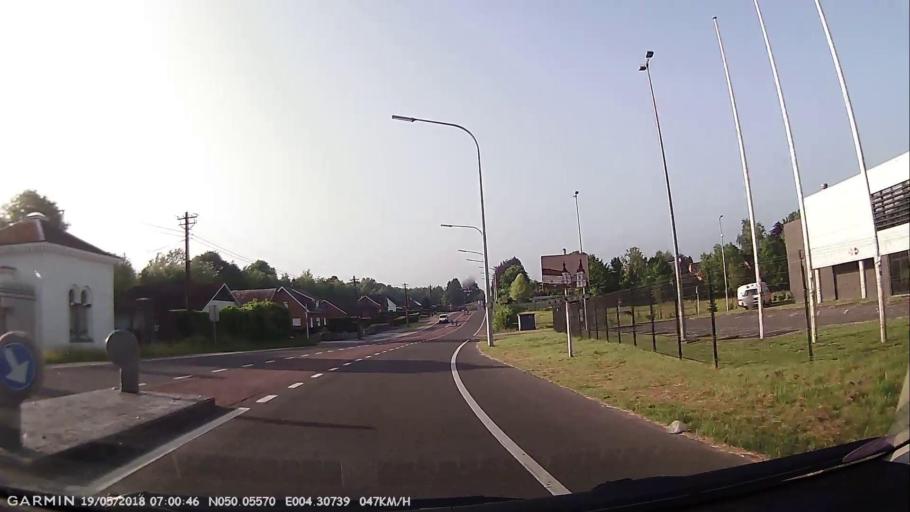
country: BE
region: Wallonia
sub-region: Province du Hainaut
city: Chimay
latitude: 50.0556
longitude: 4.3075
